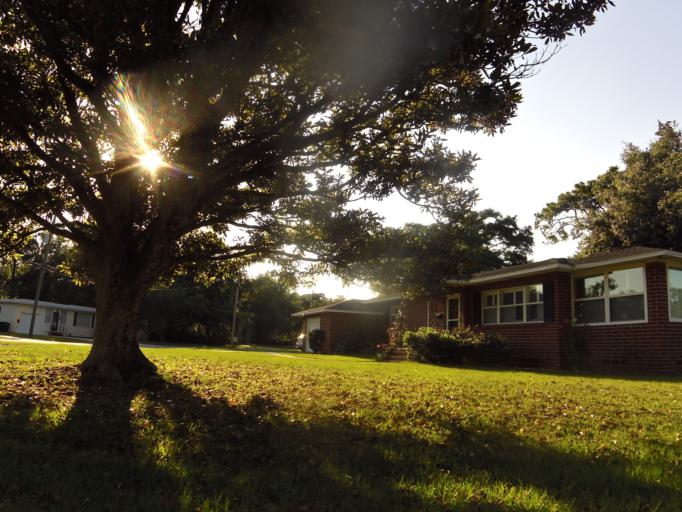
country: US
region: Florida
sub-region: Duval County
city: Jacksonville
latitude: 30.2361
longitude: -81.6176
